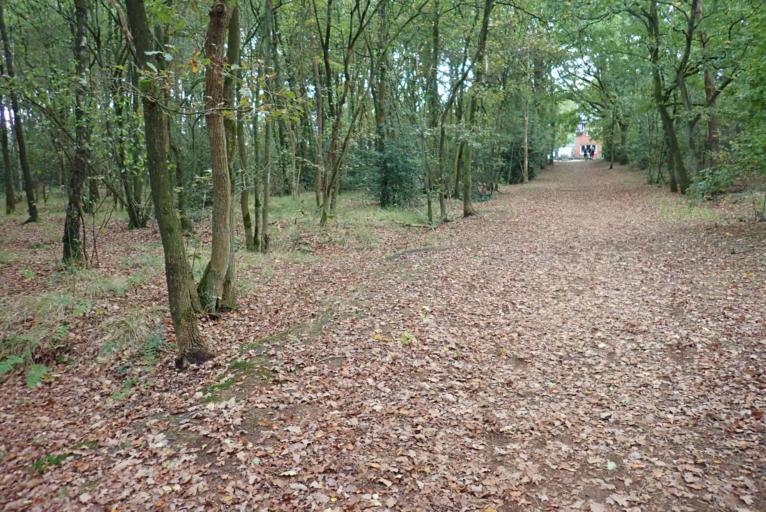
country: BE
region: Flanders
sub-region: Provincie Antwerpen
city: Essen
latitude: 51.4310
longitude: 4.4576
